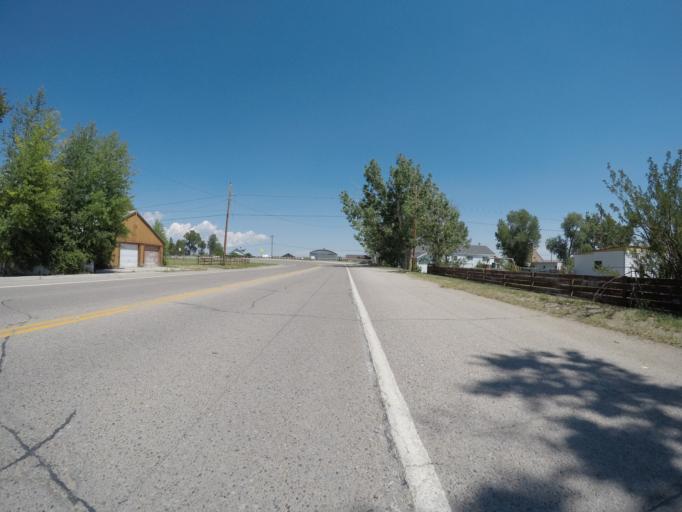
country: US
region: Wyoming
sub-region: Sublette County
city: Marbleton
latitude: 42.5394
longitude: -110.1146
